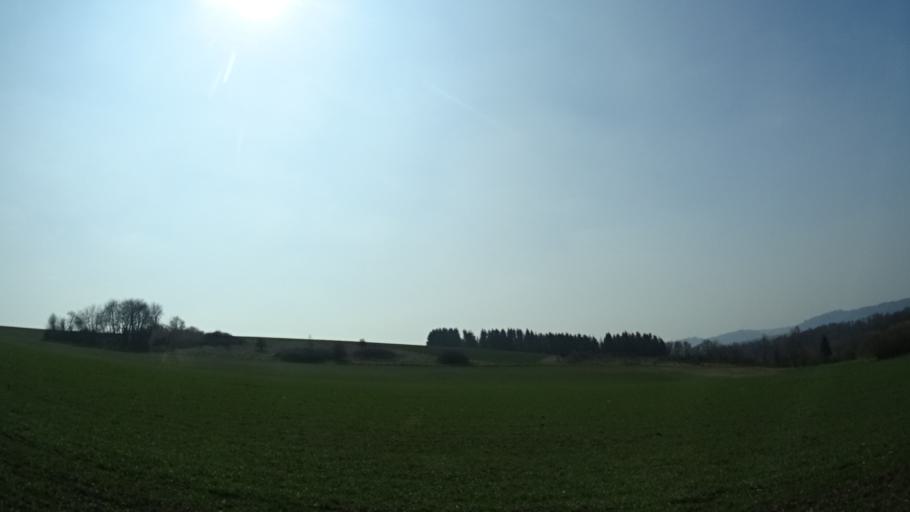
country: DE
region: Rheinland-Pfalz
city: Mettweiler
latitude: 49.5936
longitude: 7.3056
